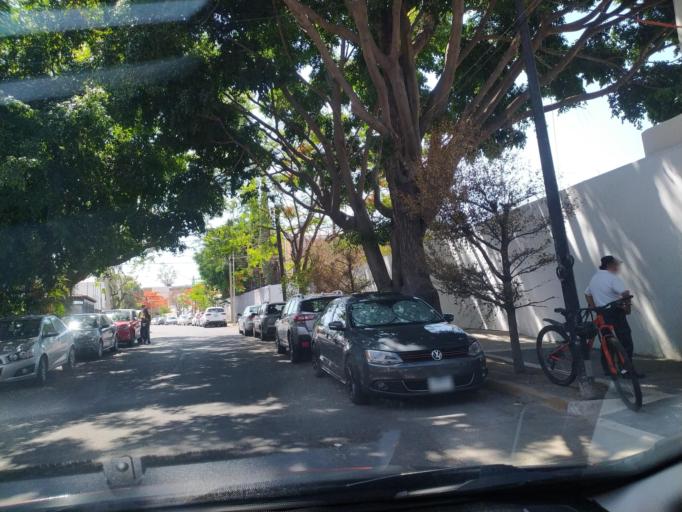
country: MX
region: Jalisco
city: Guadalajara
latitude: 20.6699
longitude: -103.3911
